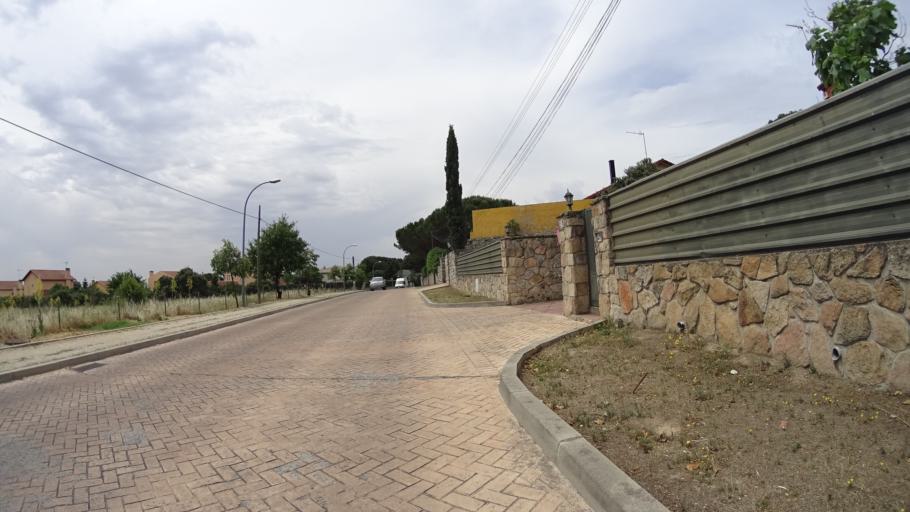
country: ES
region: Madrid
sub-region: Provincia de Madrid
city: Colmenarejo
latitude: 40.5653
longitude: -4.0101
